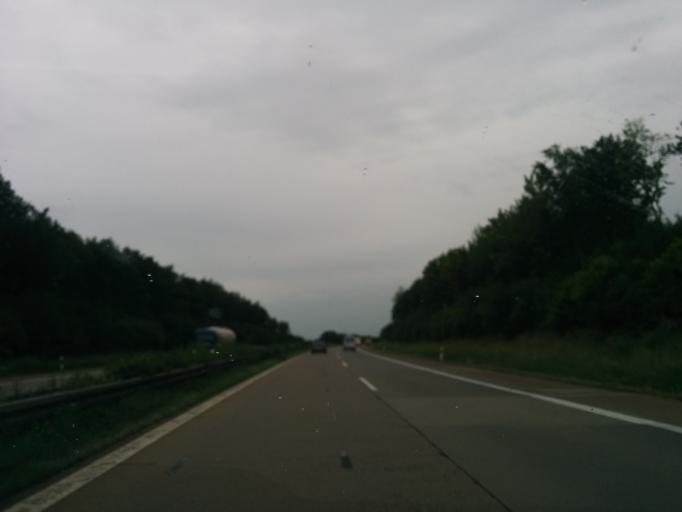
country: DE
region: Bavaria
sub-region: Regierungsbezirk Mittelfranken
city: Simmershofen
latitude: 49.5430
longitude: 10.1669
